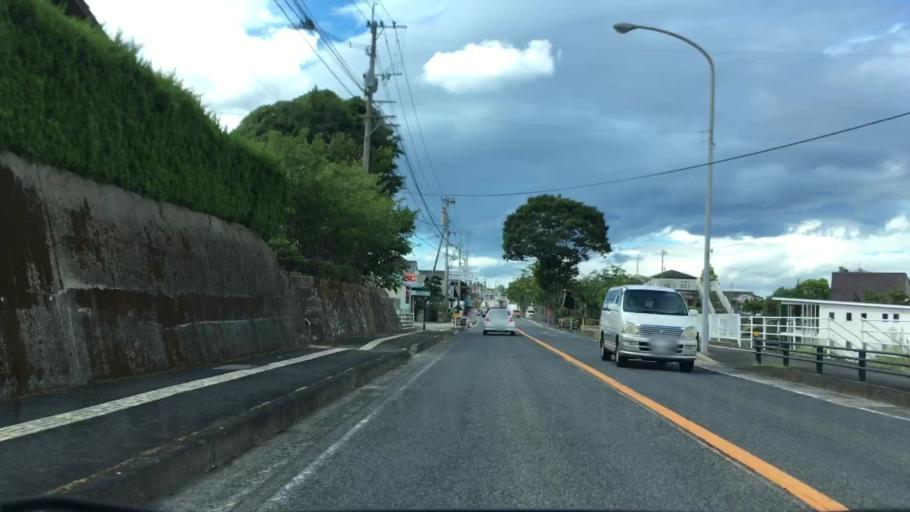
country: JP
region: Saga Prefecture
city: Imaricho-ko
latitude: 33.2083
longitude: 129.8502
